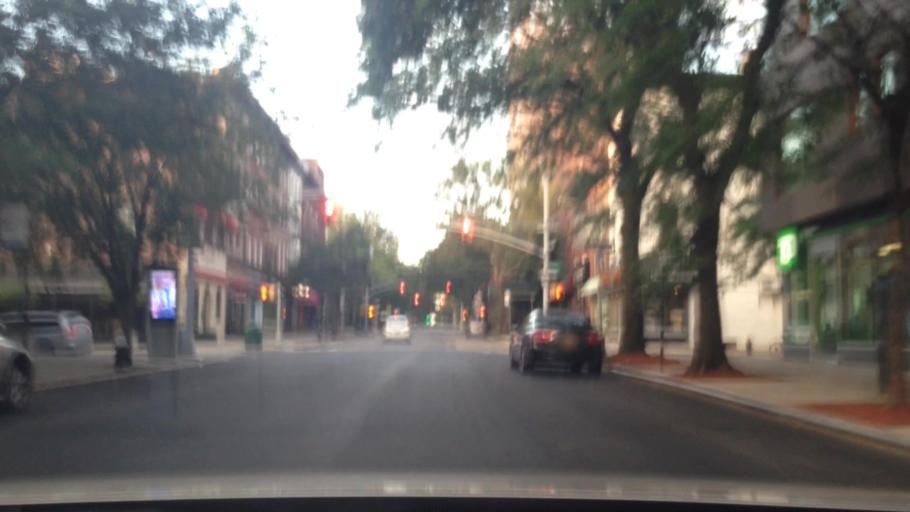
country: US
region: New York
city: New York City
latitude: 40.6827
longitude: -73.9958
